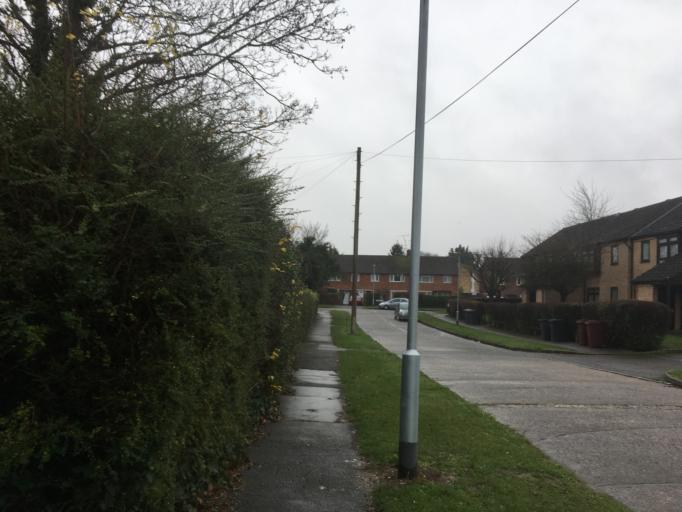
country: GB
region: England
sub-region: West Berkshire
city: Tilehurst
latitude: 51.4435
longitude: -1.0134
